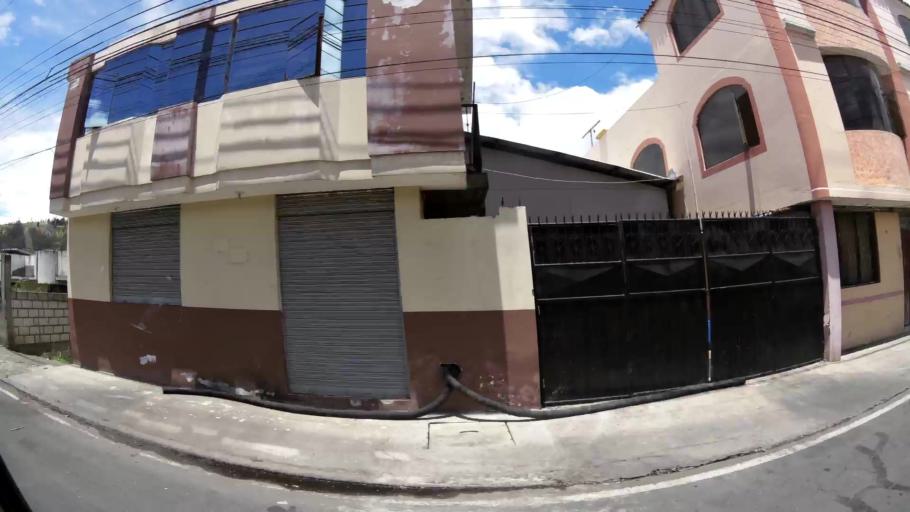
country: EC
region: Tungurahua
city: Pelileo
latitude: -1.3259
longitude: -78.5461
